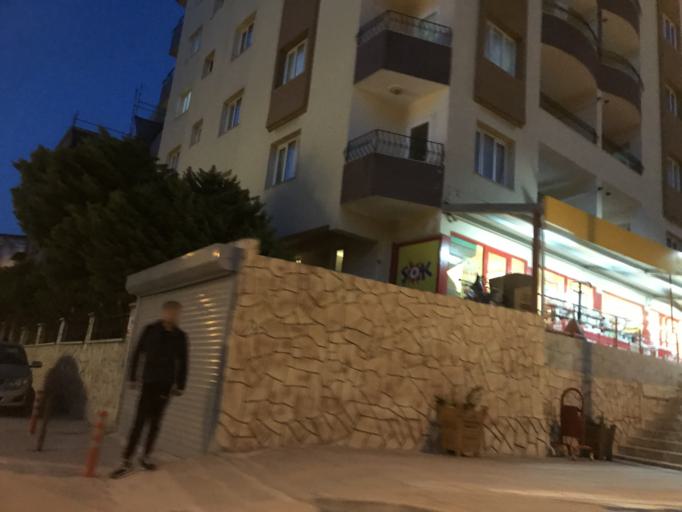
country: TR
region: Hatay
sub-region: Antakya Ilcesi
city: Antakya
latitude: 36.1959
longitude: 36.1475
